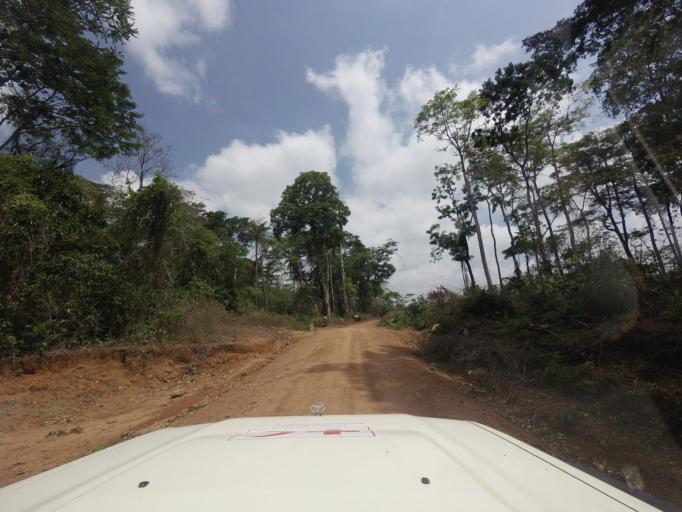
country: LR
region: Lofa
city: Voinjama
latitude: 8.4556
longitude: -9.6428
